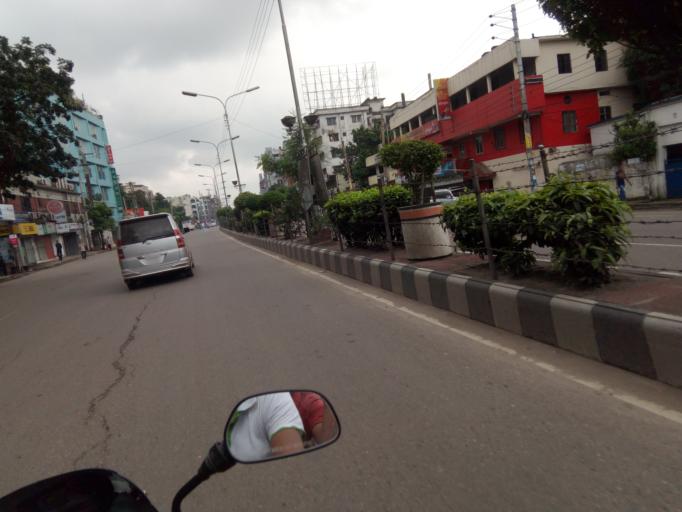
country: BD
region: Dhaka
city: Azimpur
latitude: 23.7598
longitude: 90.3895
